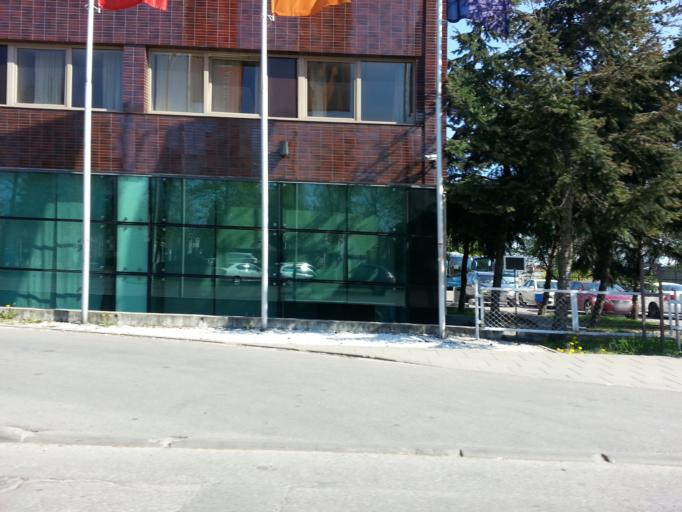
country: LT
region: Vilnius County
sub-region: Vilnius
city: Vilnius
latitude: 54.6718
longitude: 25.2852
